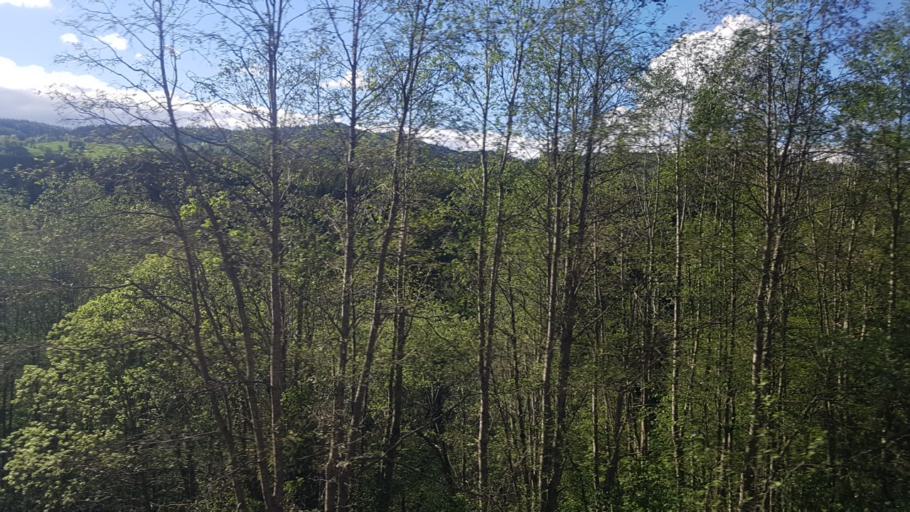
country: NO
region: Sor-Trondelag
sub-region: Midtre Gauldal
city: Storen
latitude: 62.9721
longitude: 10.2088
